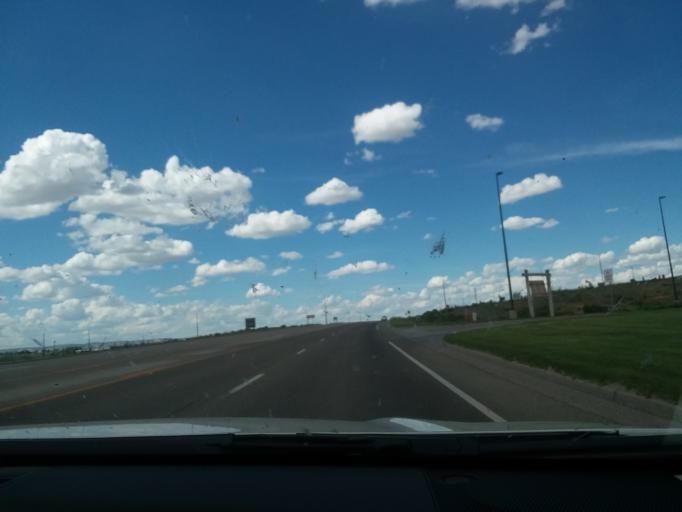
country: US
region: Wyoming
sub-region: Sweetwater County
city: North Rock Springs
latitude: 41.6248
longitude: -109.2331
